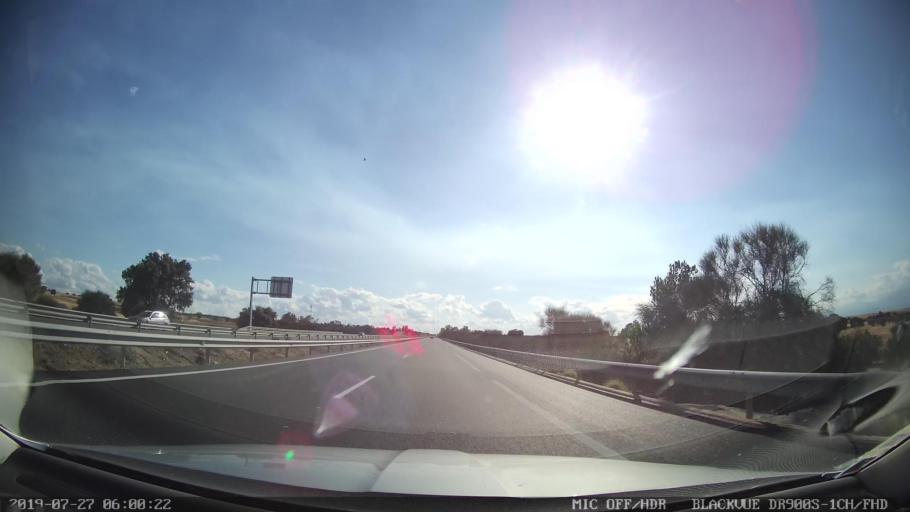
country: ES
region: Castille-La Mancha
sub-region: Province of Toledo
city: Caleruela
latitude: 39.8993
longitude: -5.2884
